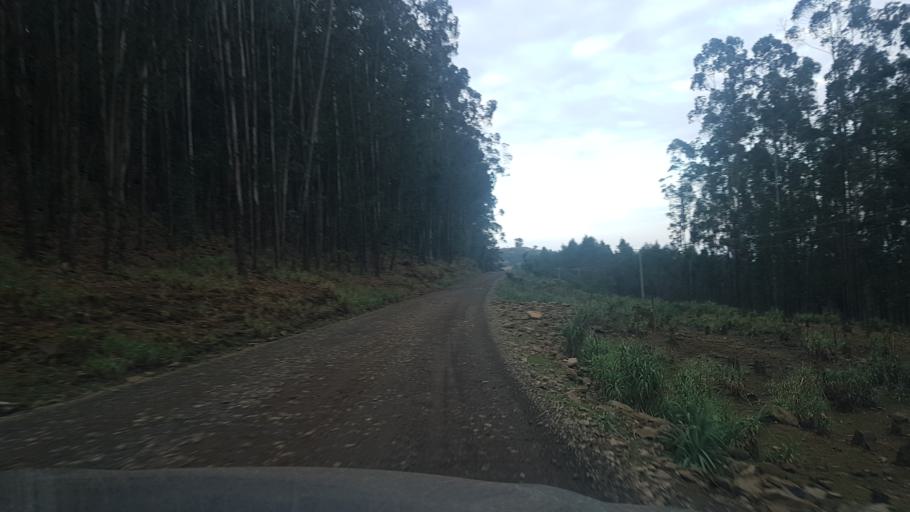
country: ET
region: Amhara
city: Finote Selam
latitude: 10.7928
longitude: 37.6640
